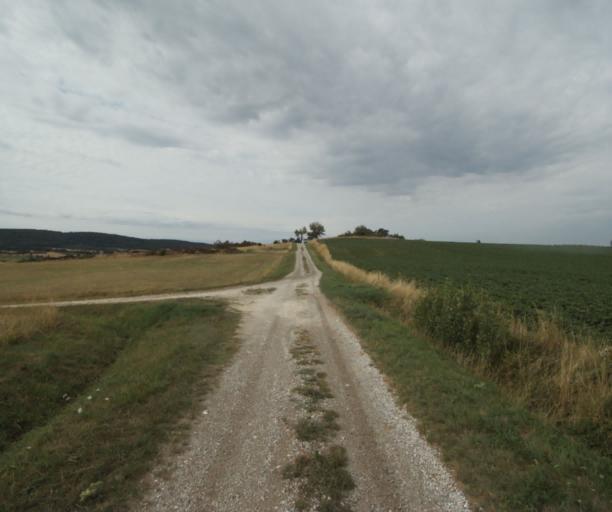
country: FR
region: Midi-Pyrenees
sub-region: Departement de la Haute-Garonne
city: Revel
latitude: 43.4272
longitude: 1.9716
